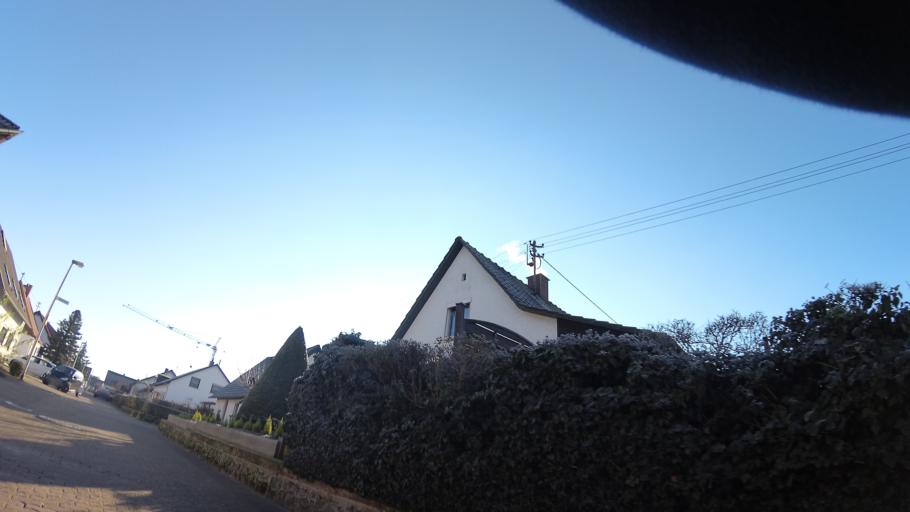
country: DE
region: Saarland
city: Saarwellingen
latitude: 49.3344
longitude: 6.7857
